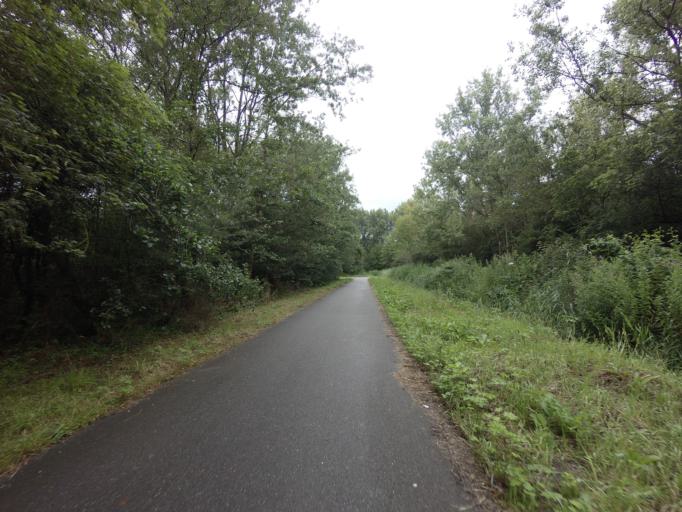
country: NL
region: North Holland
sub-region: Gemeente Velsen
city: Velsen-Zuid
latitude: 52.4367
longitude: 4.6982
